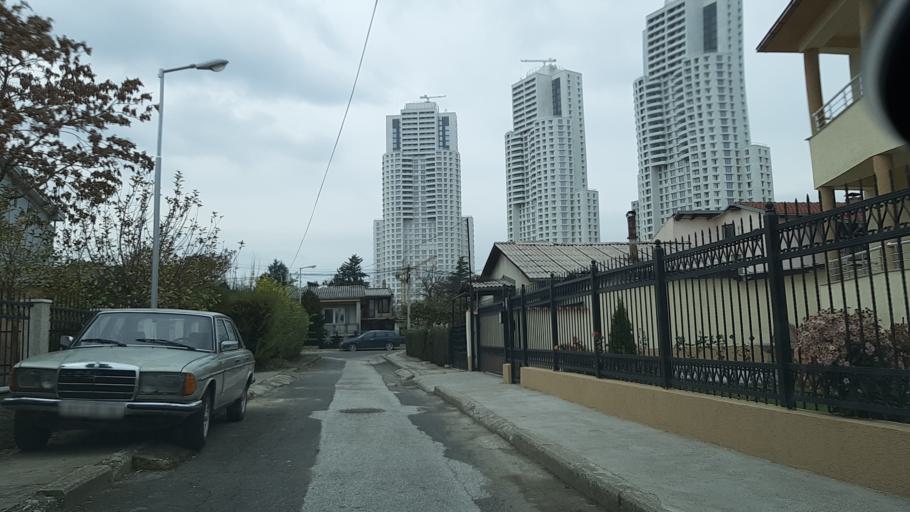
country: MK
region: Kisela Voda
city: Usje
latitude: 41.9778
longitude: 21.4686
